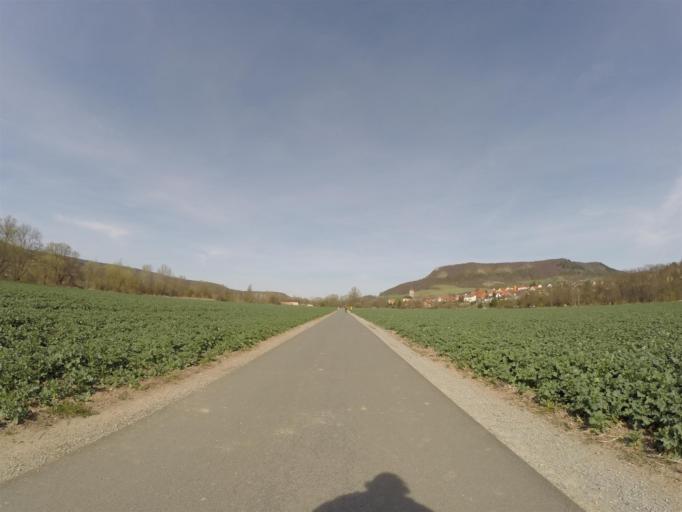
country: DE
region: Thuringia
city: Neuengonna
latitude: 50.9517
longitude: 11.6291
